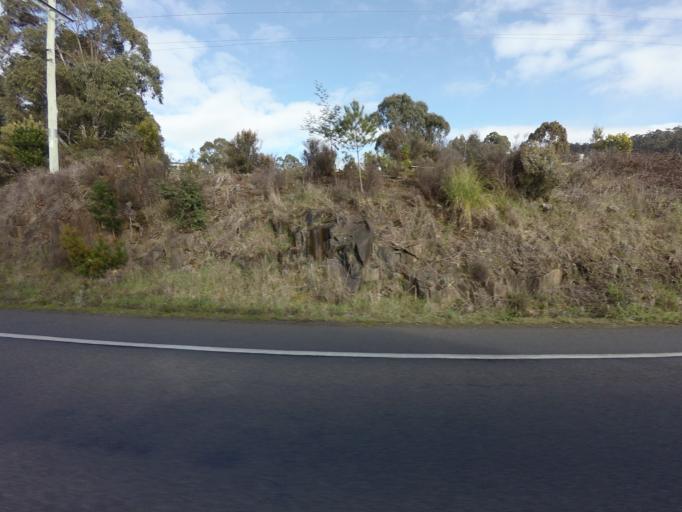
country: AU
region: Tasmania
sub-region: Huon Valley
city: Franklin
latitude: -43.1089
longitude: 147.0006
